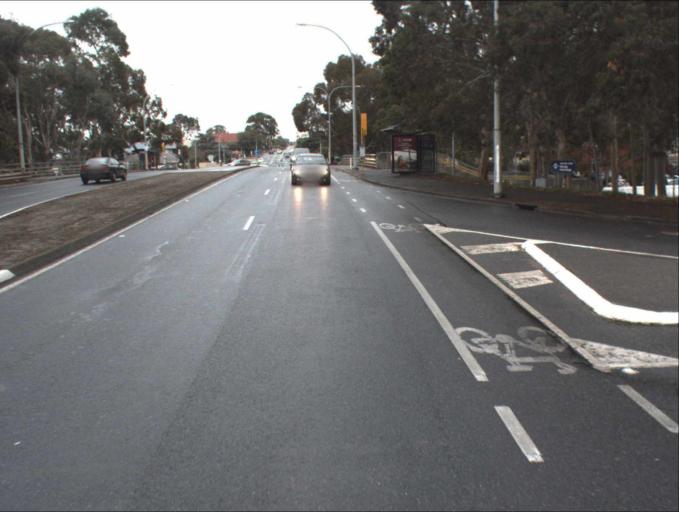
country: AU
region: South Australia
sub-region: Norwood Payneham St Peters
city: Marden
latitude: -34.8872
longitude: 138.6393
